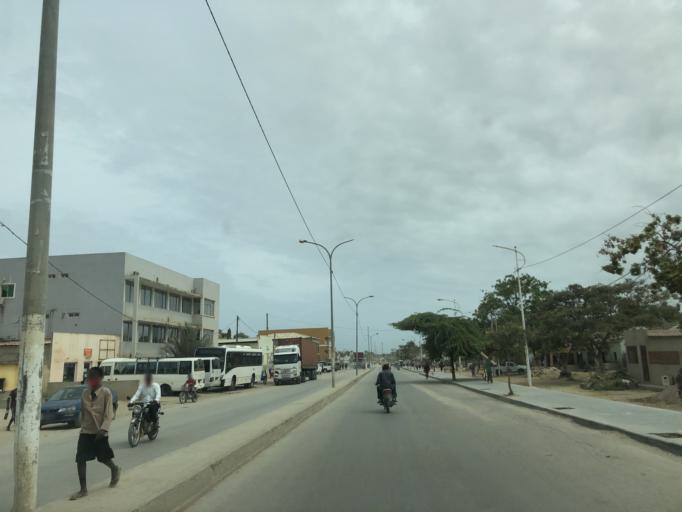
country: AO
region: Cuanza Sul
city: Sumbe
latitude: -11.2147
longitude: 13.8471
